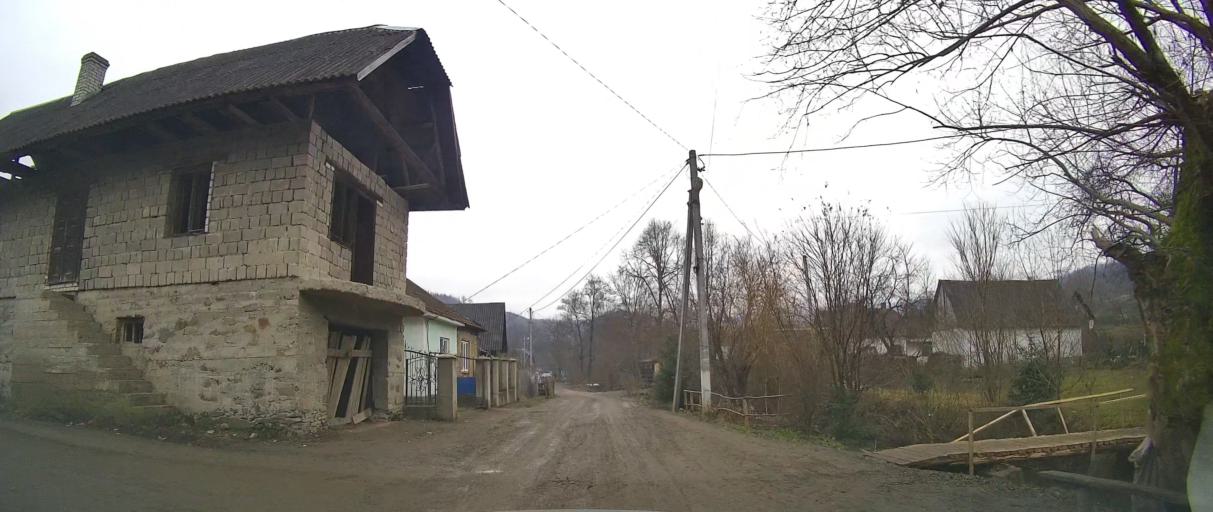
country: UA
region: Zakarpattia
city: Velykyi Bereznyi
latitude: 48.9708
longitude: 22.5494
